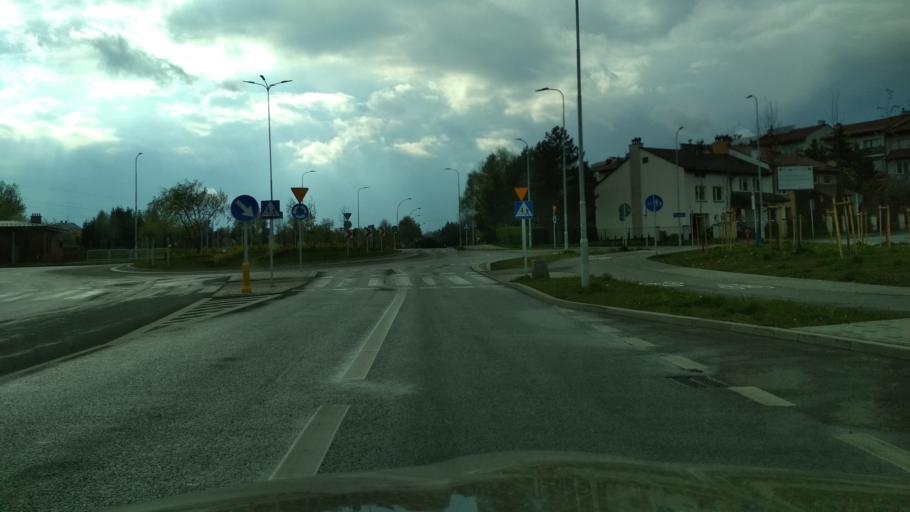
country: PL
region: Subcarpathian Voivodeship
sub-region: Rzeszow
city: Rzeszow
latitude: 50.0408
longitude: 21.9765
